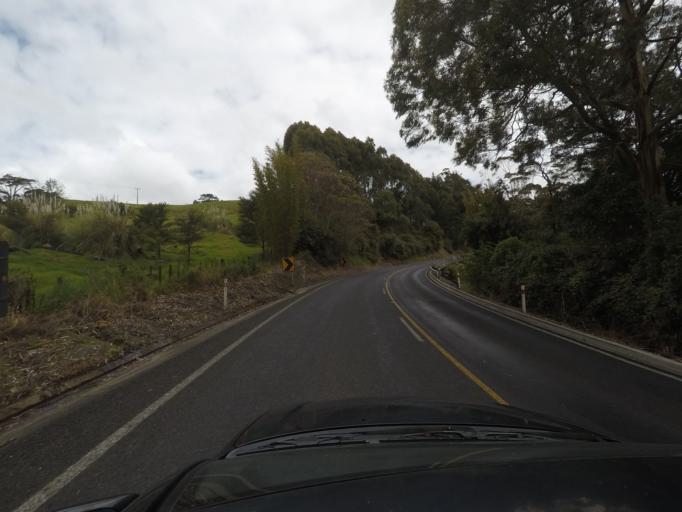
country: NZ
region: Auckland
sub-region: Auckland
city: Parakai
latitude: -36.5355
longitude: 174.4571
